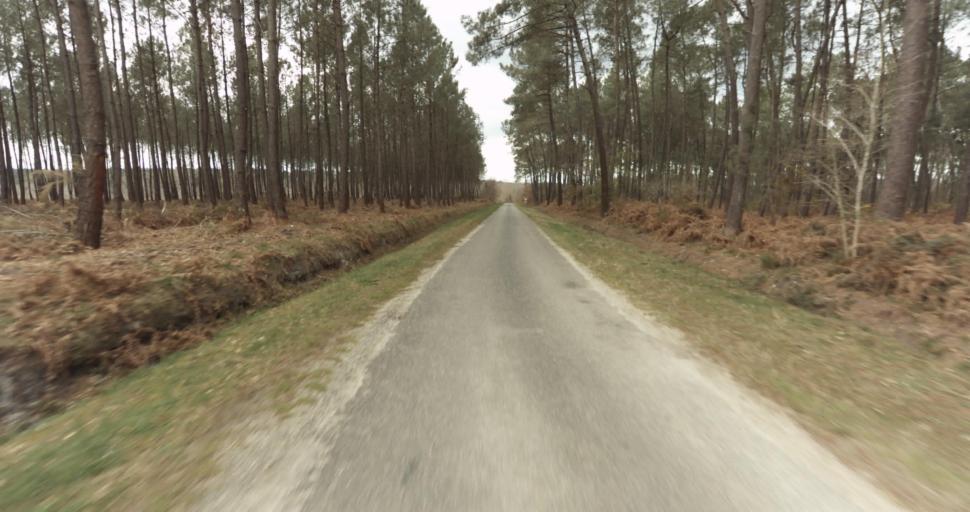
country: FR
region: Aquitaine
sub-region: Departement des Landes
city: Sarbazan
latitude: 44.0167
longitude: -0.3031
